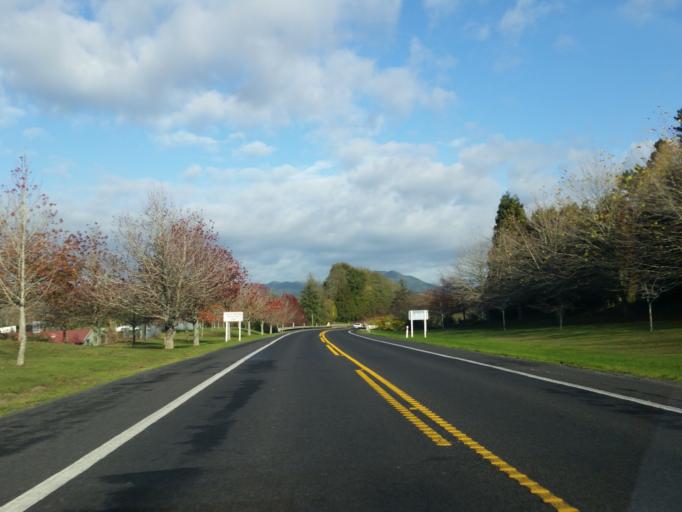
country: NZ
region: Waikato
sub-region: Hauraki District
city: Waihi
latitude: -37.4007
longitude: 175.8228
